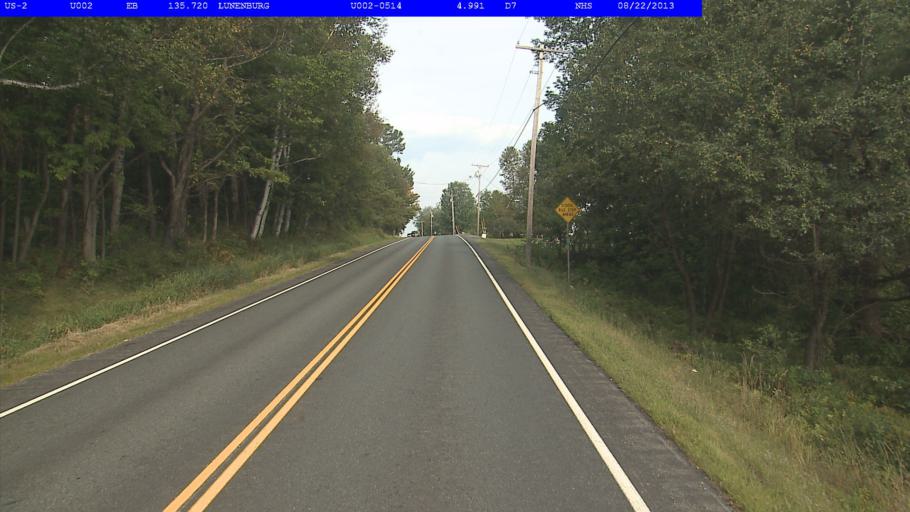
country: US
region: New Hampshire
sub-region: Coos County
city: Lancaster
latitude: 44.4634
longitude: -71.6763
